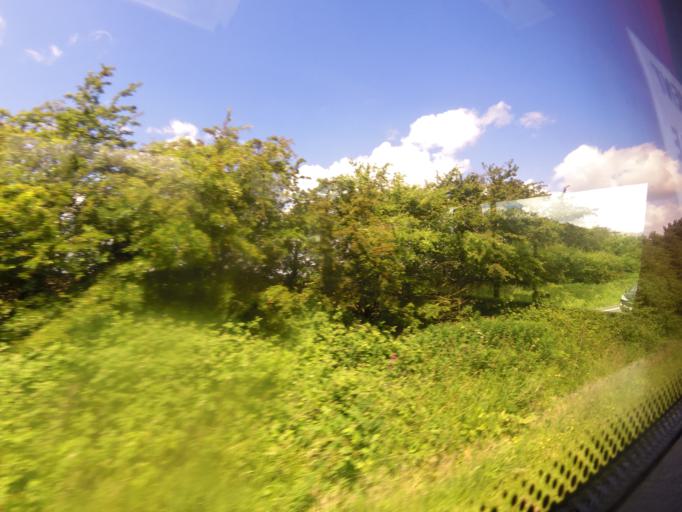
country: GB
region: England
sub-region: Norfolk
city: Aylsham
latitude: 52.7958
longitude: 1.2688
